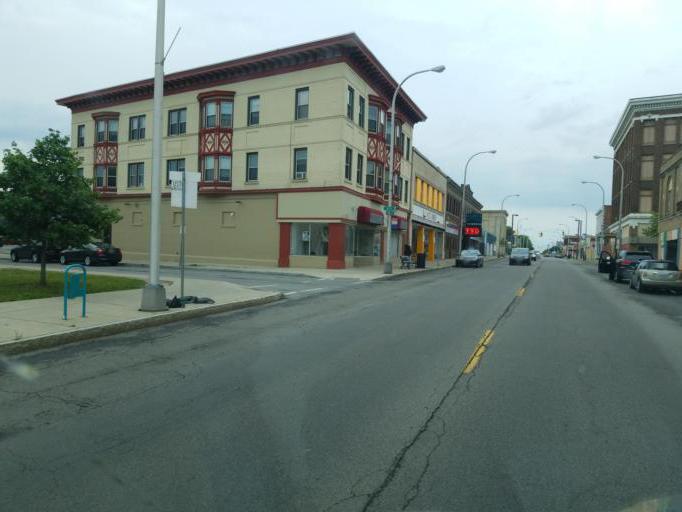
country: US
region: New York
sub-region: Niagara County
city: Niagara Falls
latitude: 43.1058
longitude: -79.0533
